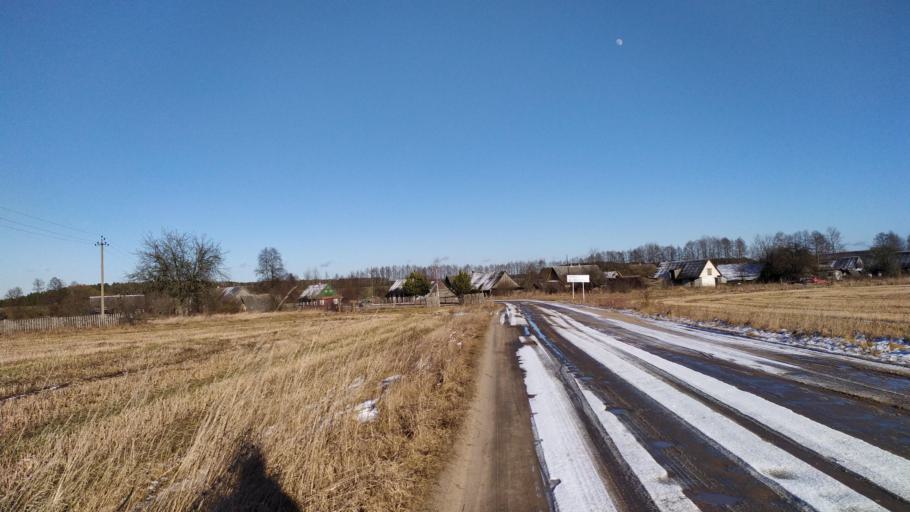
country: BY
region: Brest
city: Kamyanyets
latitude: 52.3731
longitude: 23.8837
